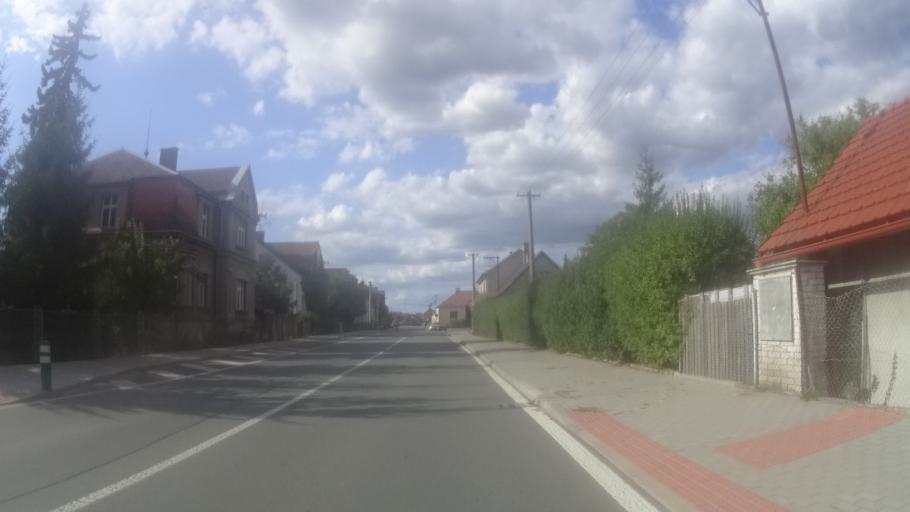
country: CZ
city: Albrechtice nad Orlici
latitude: 50.1427
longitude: 16.0621
